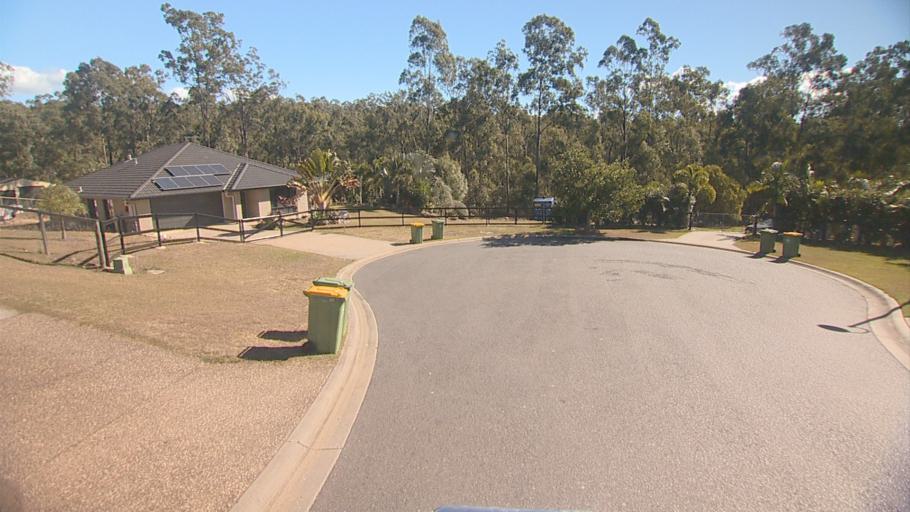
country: AU
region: Queensland
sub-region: Ipswich
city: Springfield Lakes
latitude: -27.7508
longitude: 152.9340
